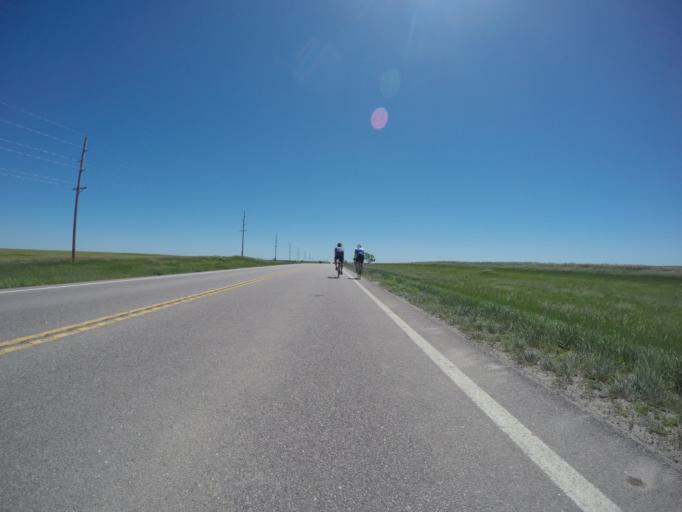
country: US
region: Kansas
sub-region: Norton County
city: Norton
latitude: 39.8284
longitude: -99.6582
